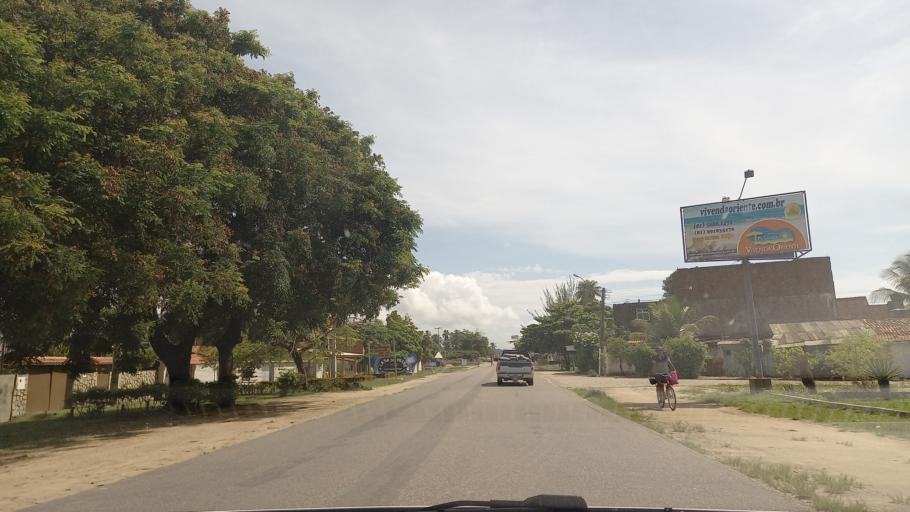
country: BR
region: Pernambuco
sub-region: Sao Jose Da Coroa Grande
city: Sao Jose da Coroa Grande
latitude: -8.9007
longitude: -35.1511
